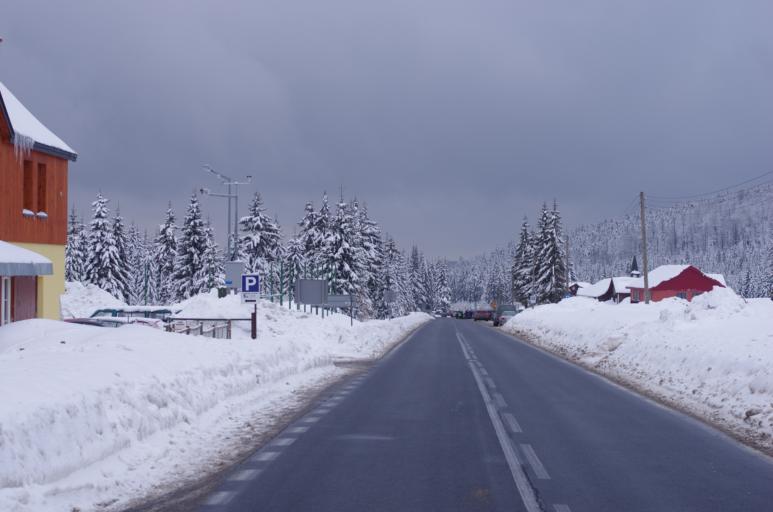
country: CZ
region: Liberecky
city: Harrachov
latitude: 50.8181
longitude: 15.4326
